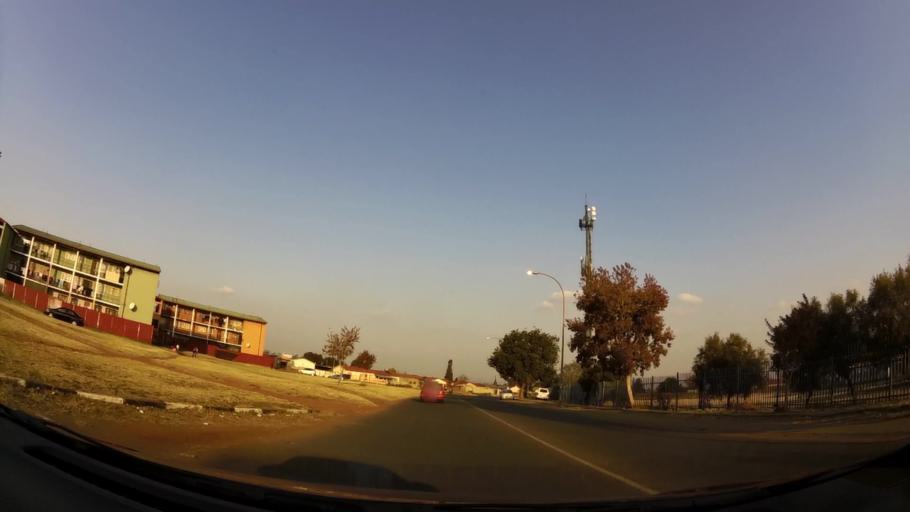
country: ZA
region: Gauteng
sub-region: City of Johannesburg Metropolitan Municipality
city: Soweto
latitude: -26.2843
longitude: 27.8998
